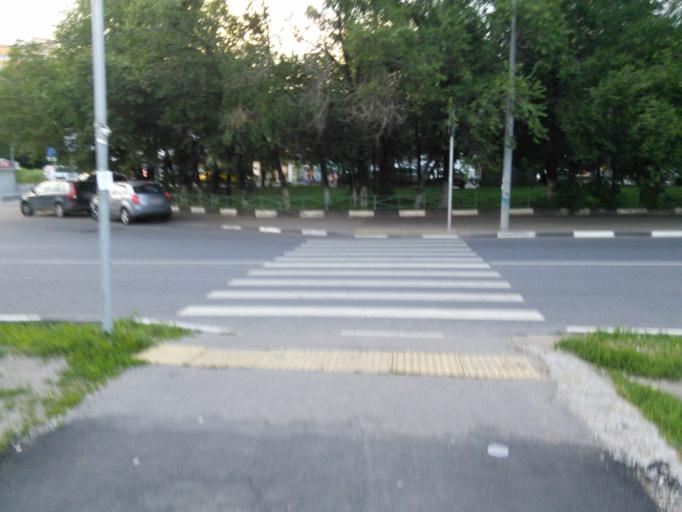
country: RU
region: Moscow
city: Tekstil'shchiki
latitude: 55.7094
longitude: 37.7452
